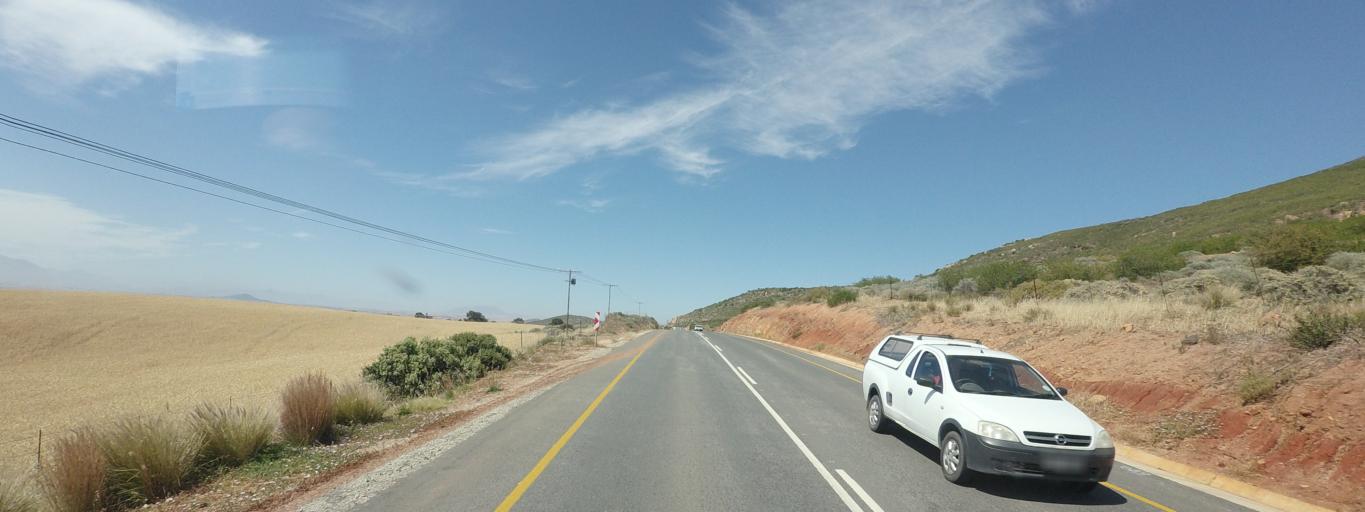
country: ZA
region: Western Cape
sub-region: West Coast District Municipality
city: Piketberg
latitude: -32.9269
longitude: 18.7560
